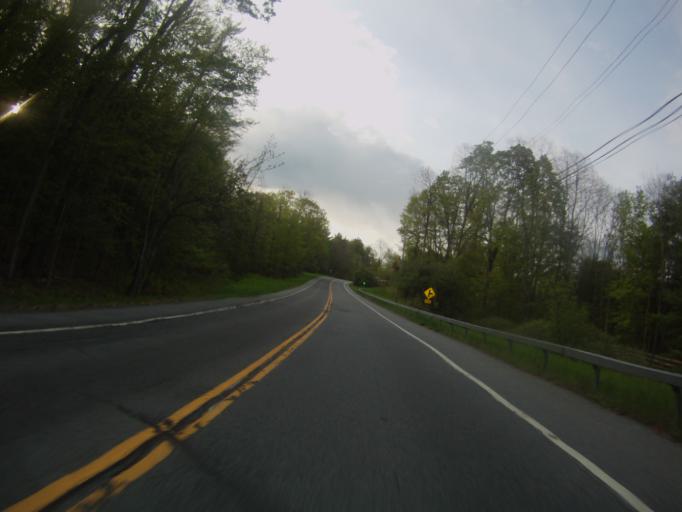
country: US
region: New York
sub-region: Essex County
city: Ticonderoga
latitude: 43.7960
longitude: -73.4857
